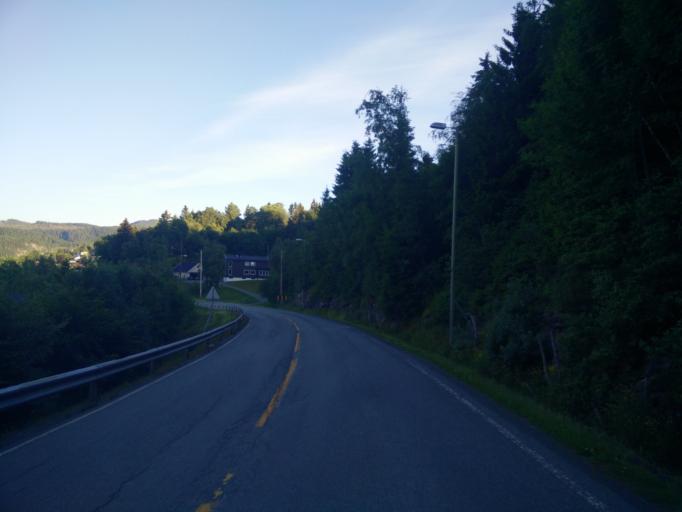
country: NO
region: Sor-Trondelag
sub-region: Skaun
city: Borsa
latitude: 63.3399
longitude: 10.0568
